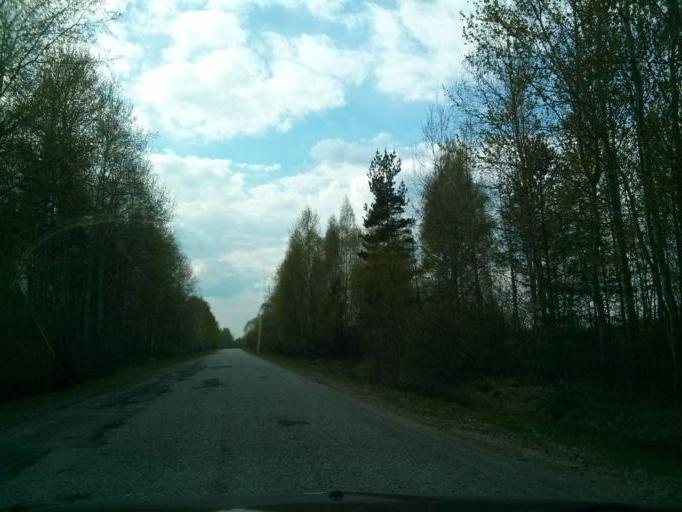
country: RU
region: Nizjnij Novgorod
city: Shimorskoye
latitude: 55.3397
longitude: 41.8729
